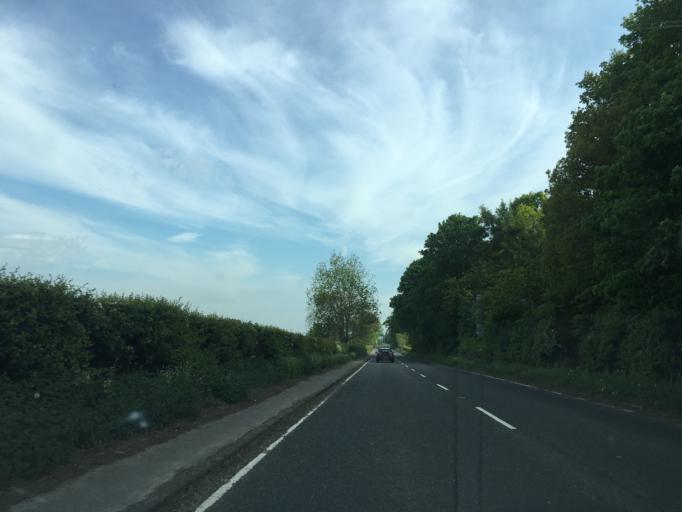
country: GB
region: Scotland
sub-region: Midlothian
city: Loanhead
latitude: 55.8677
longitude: -3.1887
